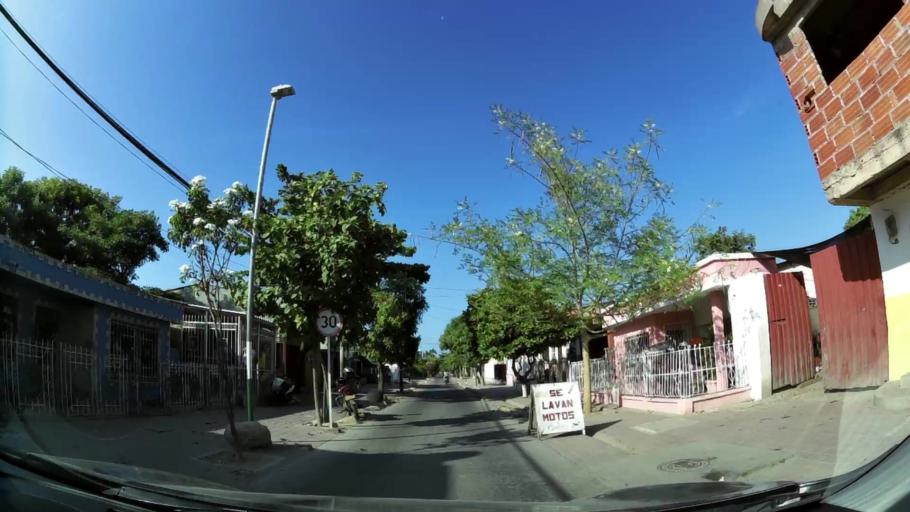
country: CO
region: Bolivar
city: Cartagena
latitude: 10.4095
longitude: -75.4964
